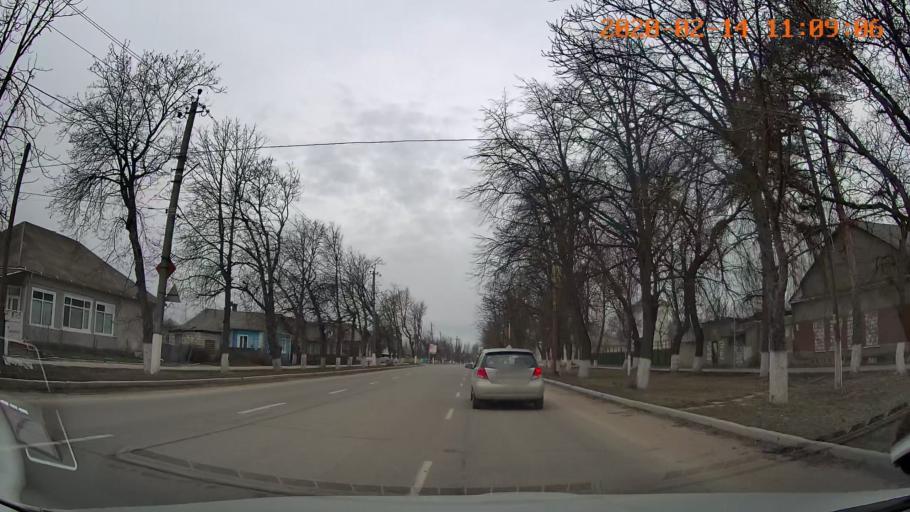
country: MD
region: Raionul Edinet
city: Edinet
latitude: 48.1760
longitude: 27.2965
